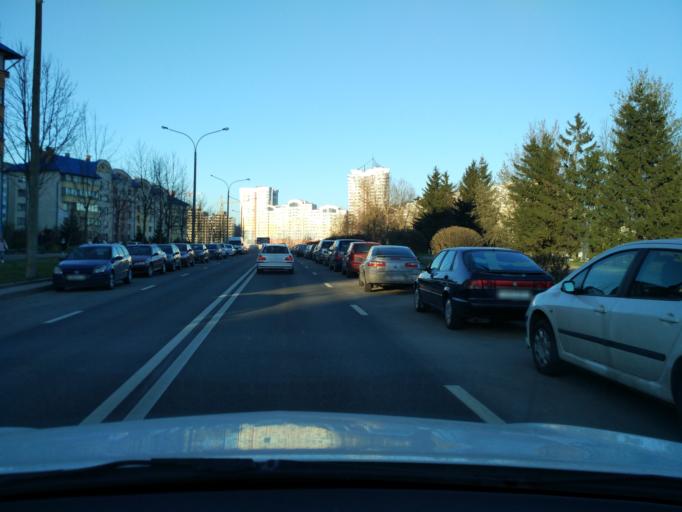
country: BY
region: Minsk
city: Shchomyslitsa
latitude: 53.8445
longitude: 27.4660
